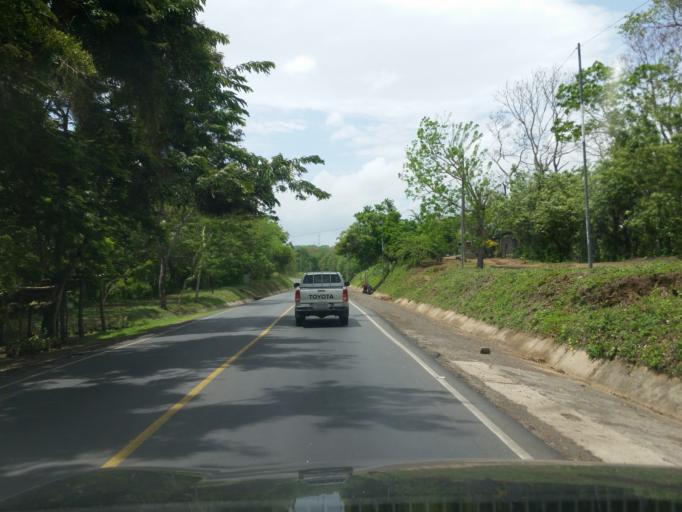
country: NI
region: Masaya
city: Catarina
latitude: 11.9249
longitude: -86.0866
